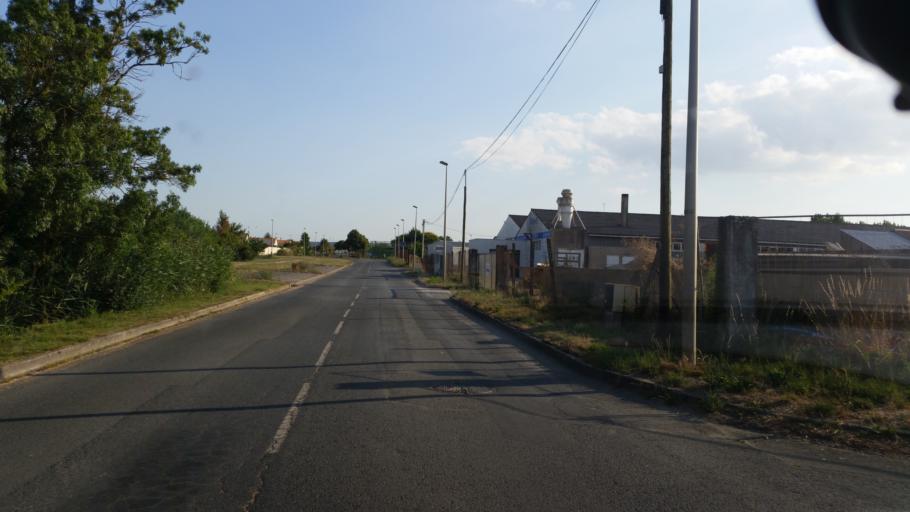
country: FR
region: Poitou-Charentes
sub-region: Departement de la Charente-Maritime
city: Marans
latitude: 46.3111
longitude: -1.0048
